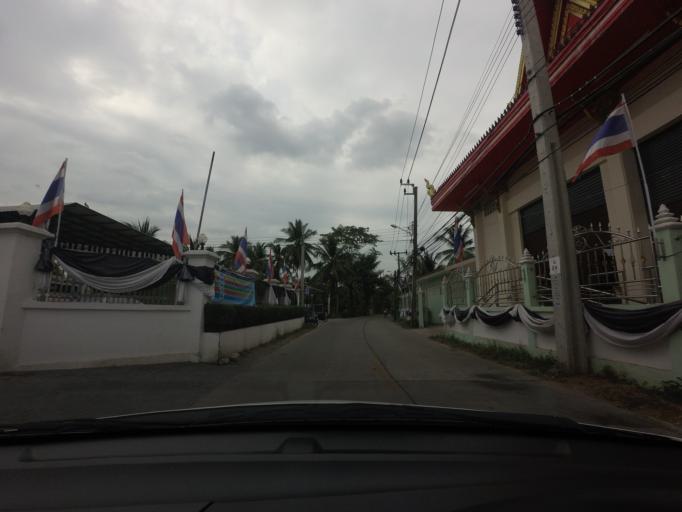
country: TH
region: Bangkok
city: Yan Nawa
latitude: 13.6882
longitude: 100.5631
